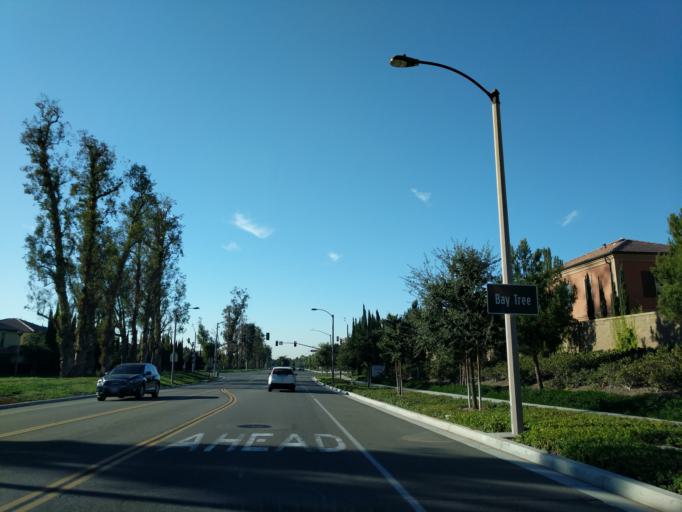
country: US
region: California
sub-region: Orange County
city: Irvine
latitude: 33.6890
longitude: -117.7580
